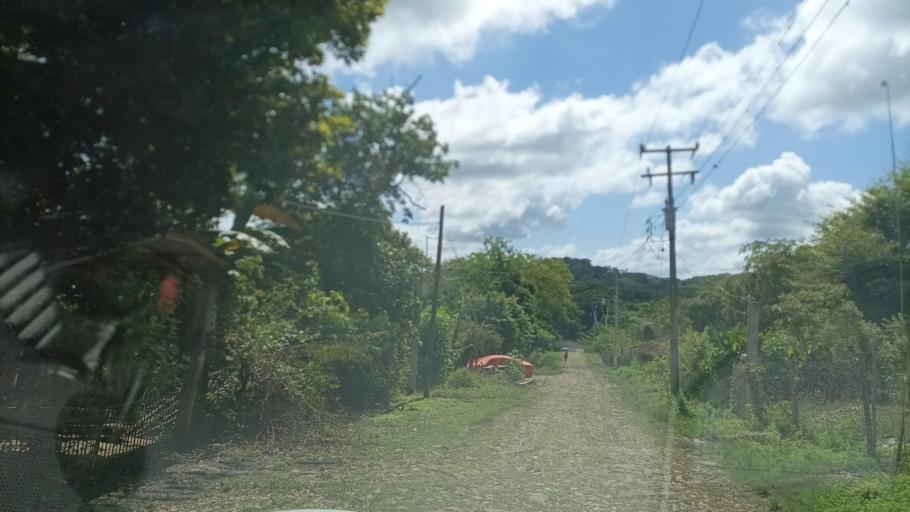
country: MX
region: Veracruz
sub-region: Tantoyuca
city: El Lindero
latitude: 21.1893
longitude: -98.1480
